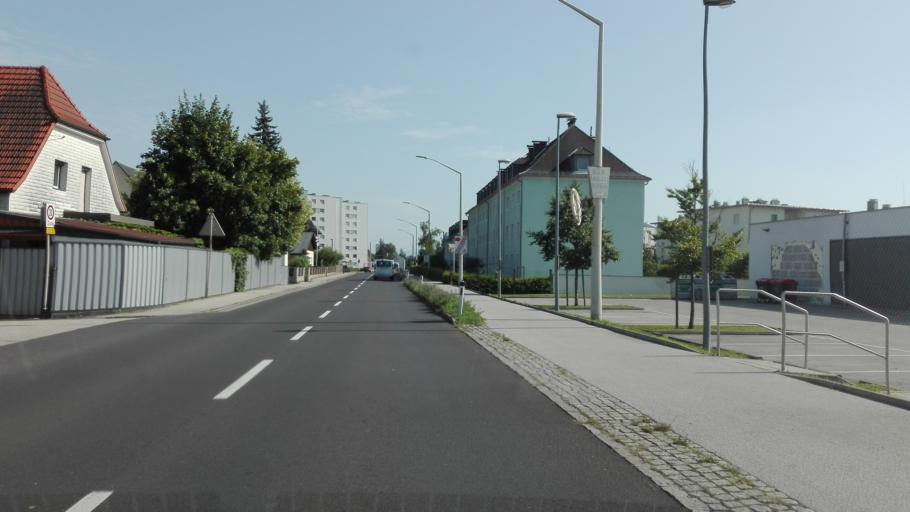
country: AT
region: Upper Austria
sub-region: Politischer Bezirk Linz-Land
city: Traun
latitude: 48.2476
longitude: 14.2594
